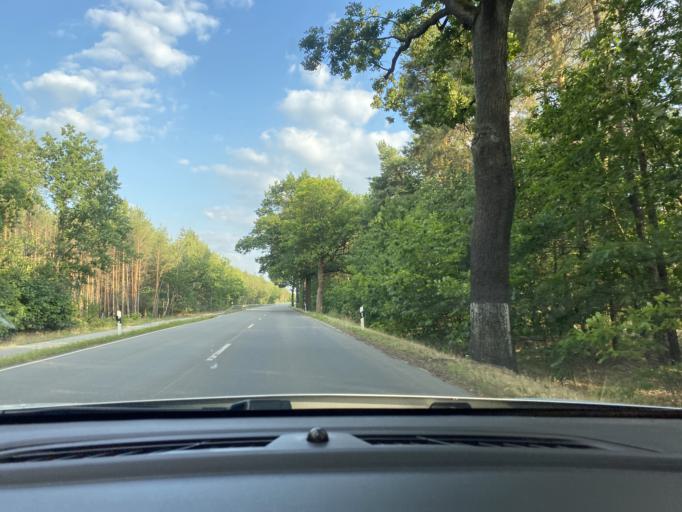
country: DE
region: Saxony
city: Wittichenau
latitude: 51.4127
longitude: 14.2869
